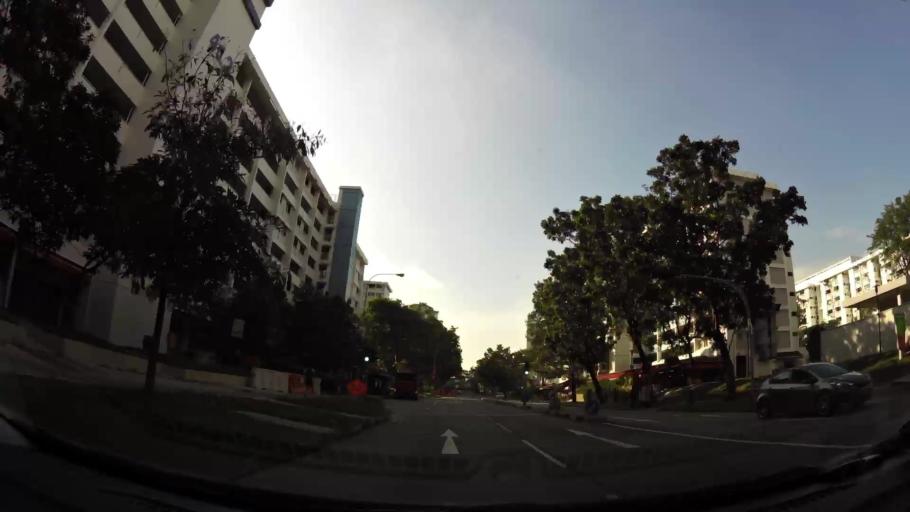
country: SG
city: Singapore
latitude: 1.3294
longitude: 103.9308
